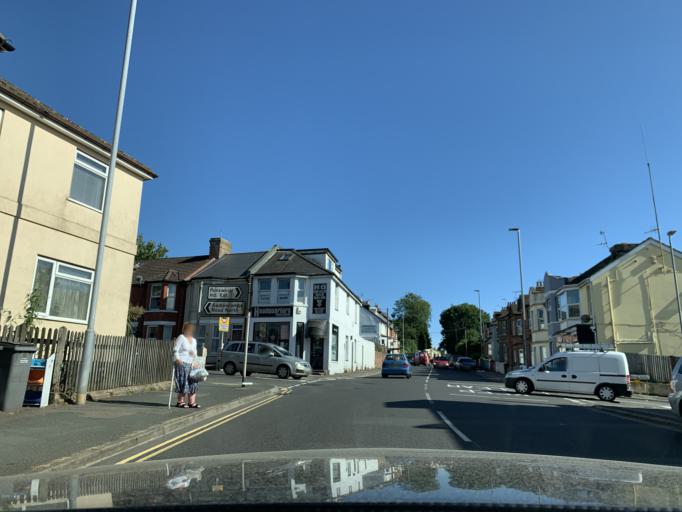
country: GB
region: England
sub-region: East Sussex
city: Saint Leonards-on-Sea
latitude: 50.8716
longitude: 0.5546
